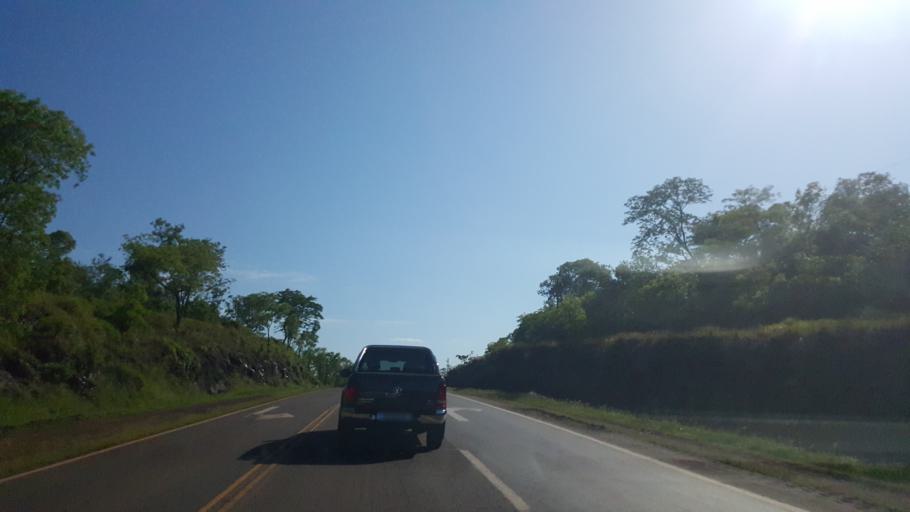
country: AR
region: Misiones
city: Santa Ana
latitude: -27.3569
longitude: -55.5557
